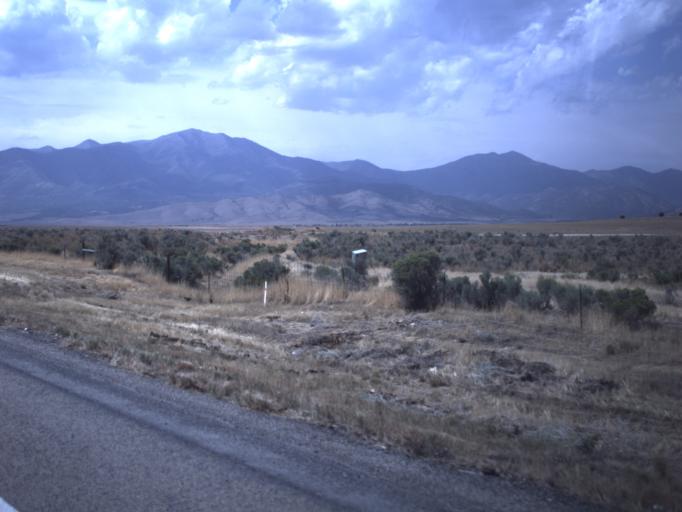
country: US
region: Utah
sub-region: Utah County
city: Eagle Mountain
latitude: 40.3744
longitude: -112.0163
